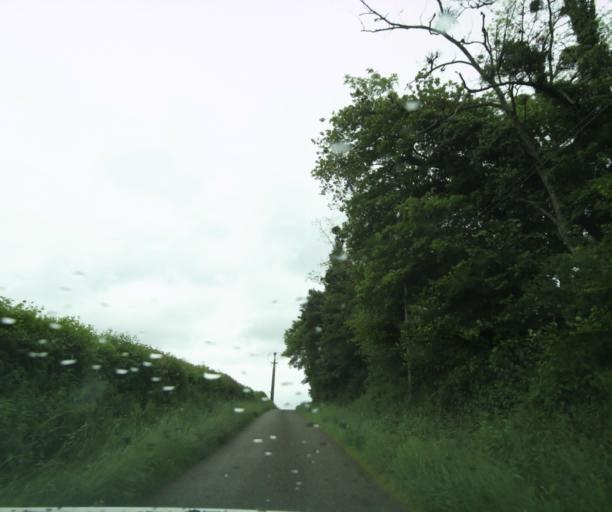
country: FR
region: Bourgogne
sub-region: Departement de Saone-et-Loire
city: Charolles
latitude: 46.4883
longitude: 4.2667
